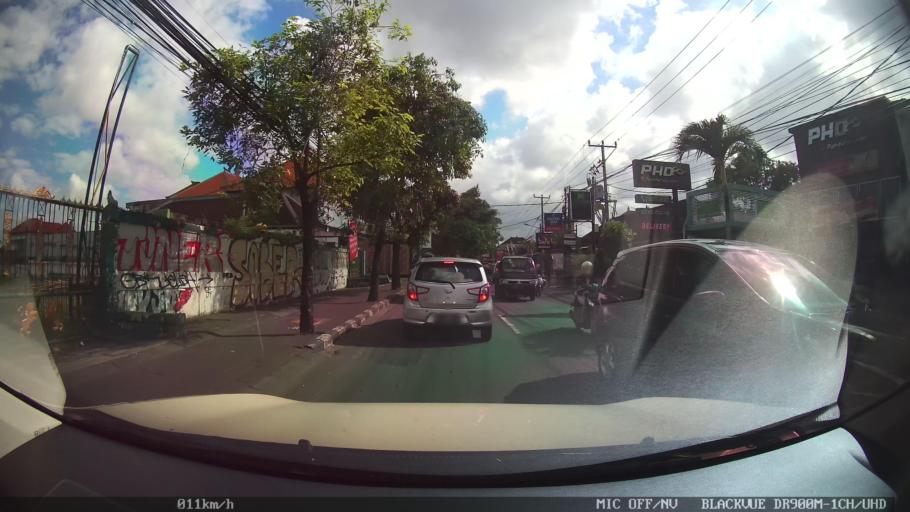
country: ID
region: Bali
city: Kuta
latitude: -8.6760
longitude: 115.1647
